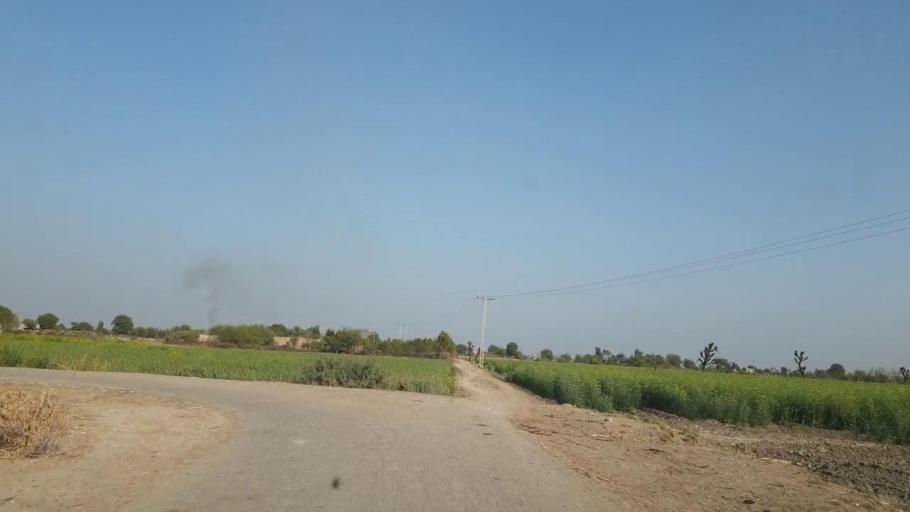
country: PK
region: Sindh
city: Tando Mittha Khan
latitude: 25.7517
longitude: 69.2003
